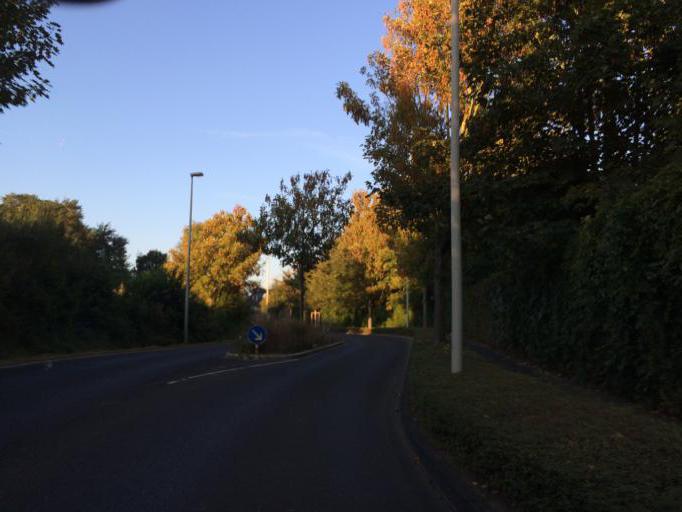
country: DE
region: North Rhine-Westphalia
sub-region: Regierungsbezirk Koln
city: Konigswinter
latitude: 50.6598
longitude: 7.1721
